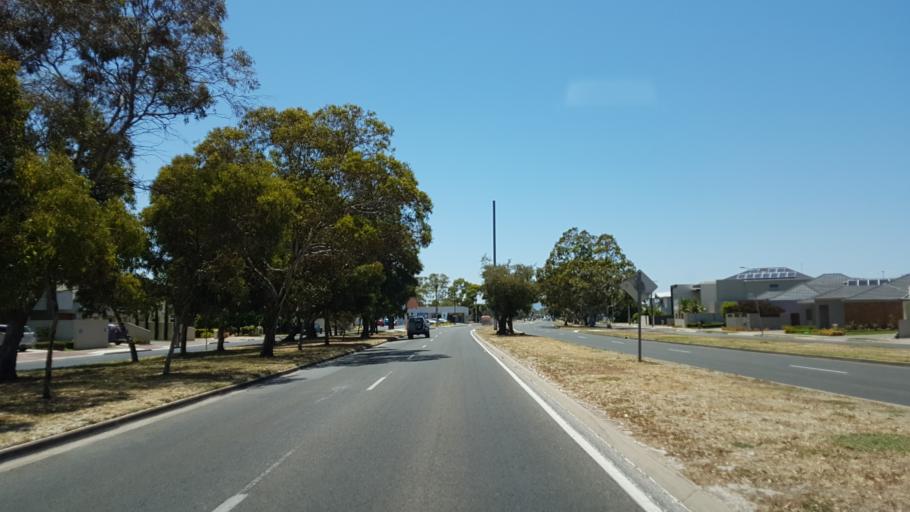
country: AU
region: South Australia
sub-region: Charles Sturt
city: Henley Beach
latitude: -34.9361
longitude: 138.5065
